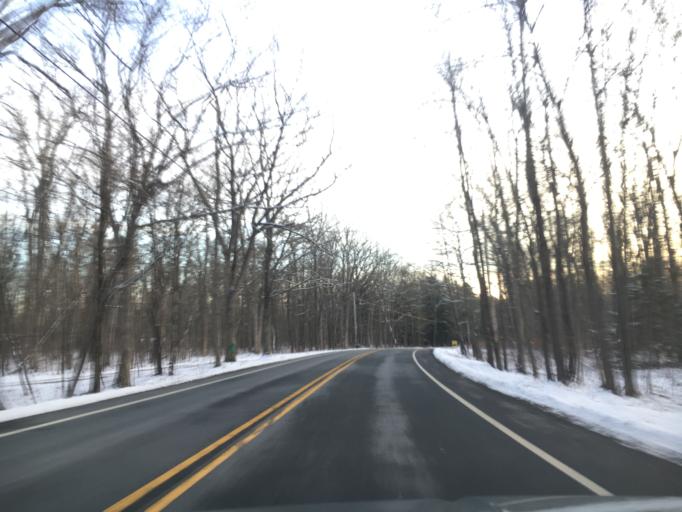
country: US
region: Pennsylvania
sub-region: Pike County
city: Saw Creek
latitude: 41.2175
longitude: -75.0806
